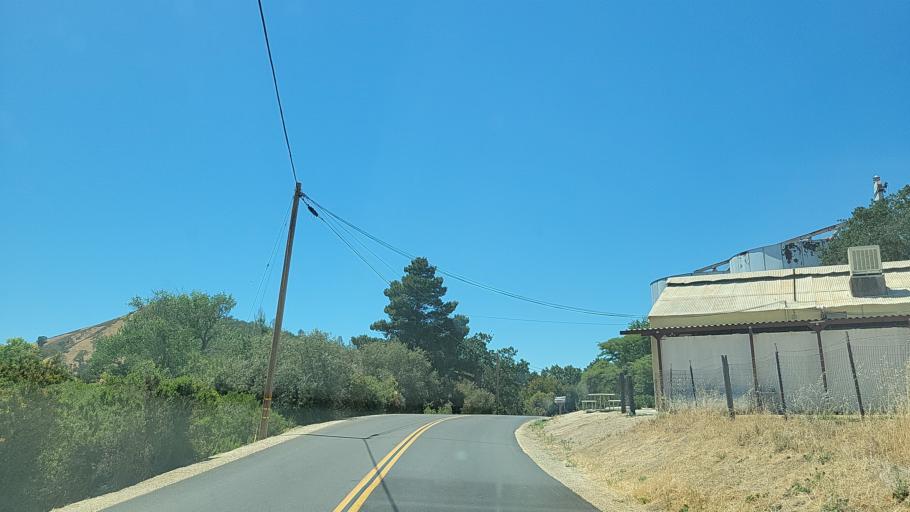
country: US
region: California
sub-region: San Luis Obispo County
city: Atascadero
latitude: 35.4913
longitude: -120.6426
